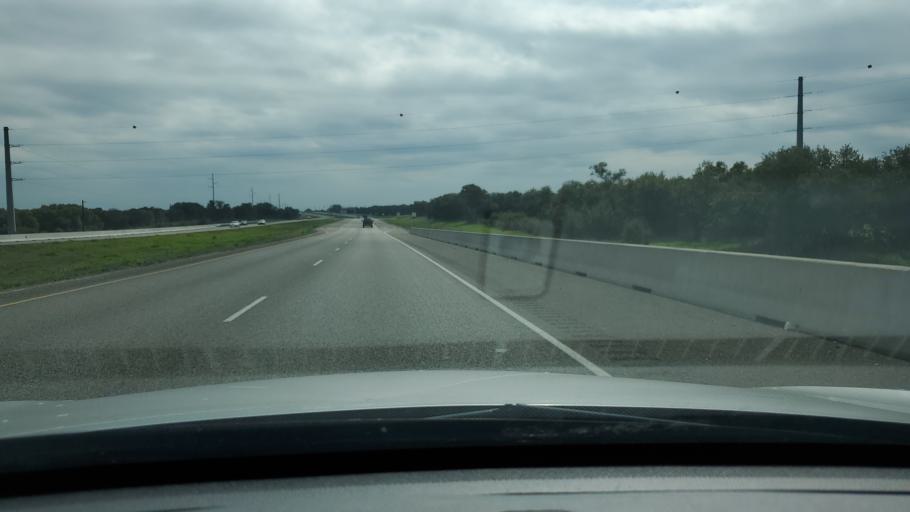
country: US
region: Texas
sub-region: Williamson County
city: Serenada
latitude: 30.7542
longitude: -97.7176
